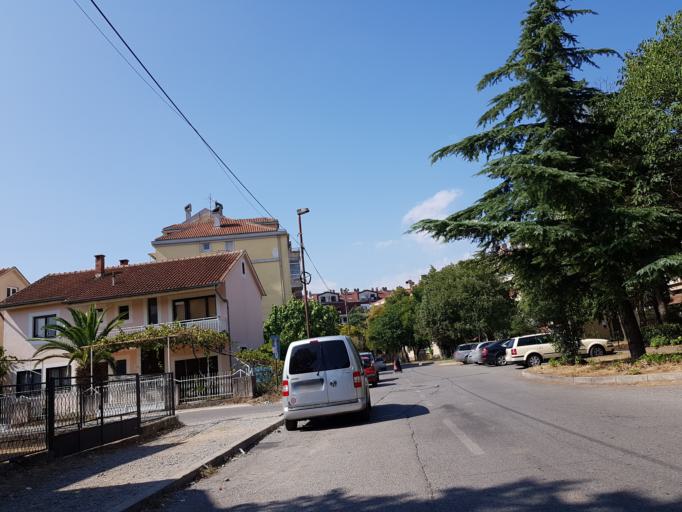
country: ME
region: Podgorica
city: Podgorica
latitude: 42.4327
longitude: 19.2770
